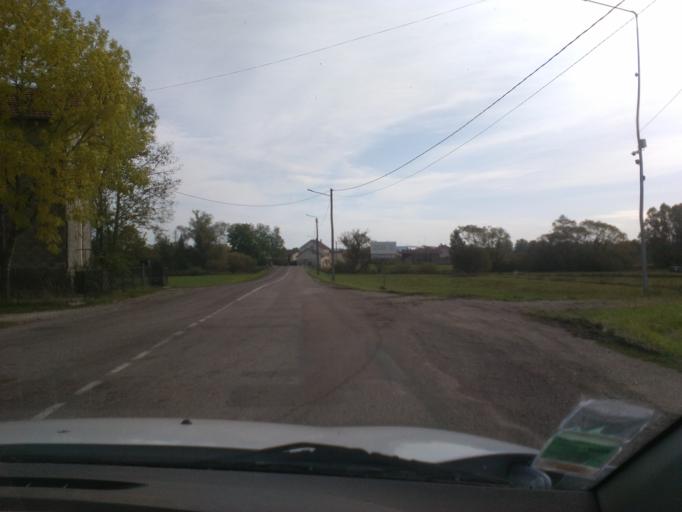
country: FR
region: Lorraine
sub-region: Departement des Vosges
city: Rambervillers
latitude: 48.3462
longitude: 6.6217
